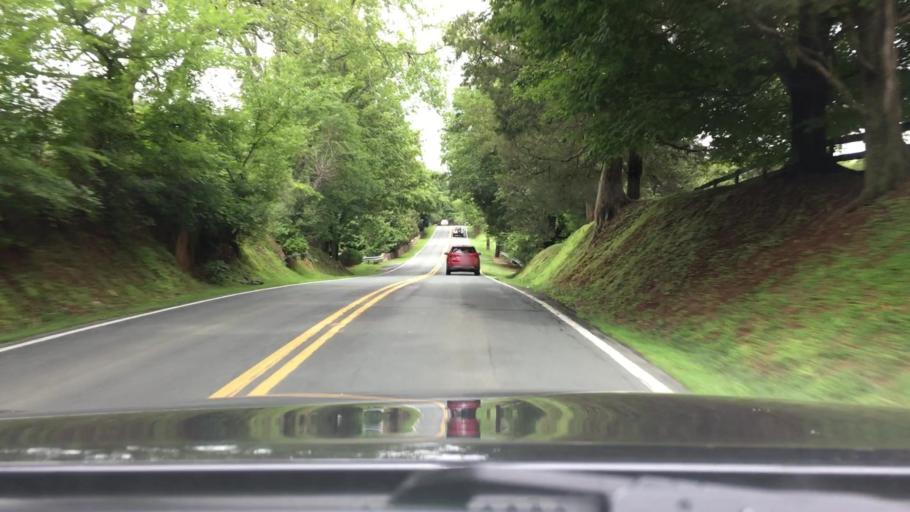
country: US
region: Virginia
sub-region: Fluvanna County
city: Lake Monticello
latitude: 38.0280
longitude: -78.3516
